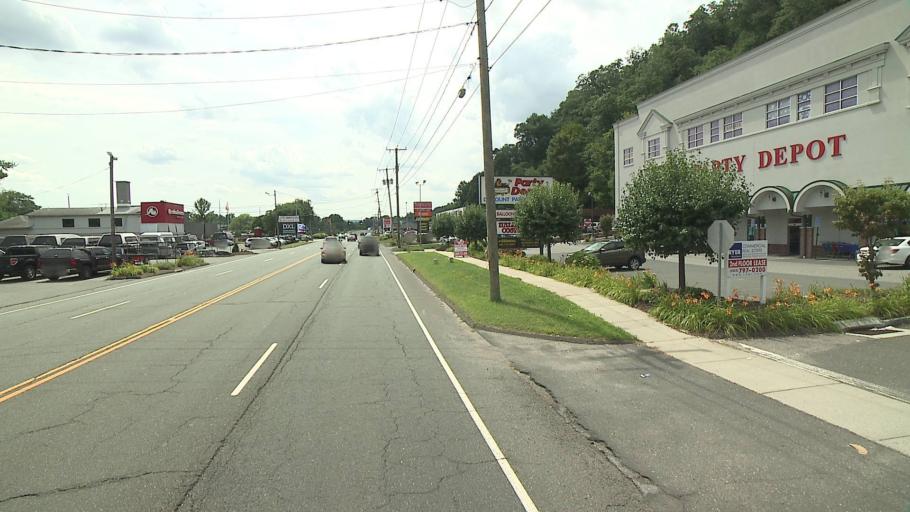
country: US
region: Connecticut
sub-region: Fairfield County
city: Danbury
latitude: 41.4304
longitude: -73.4158
